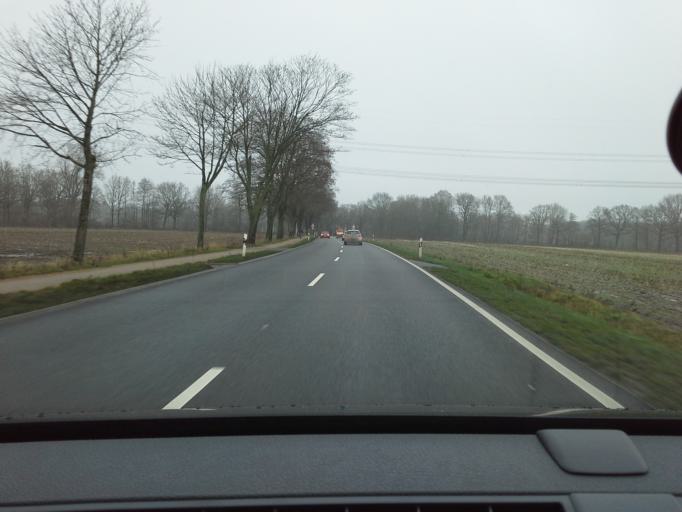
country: DE
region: Schleswig-Holstein
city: Ellerau
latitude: 53.7429
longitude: 9.9092
